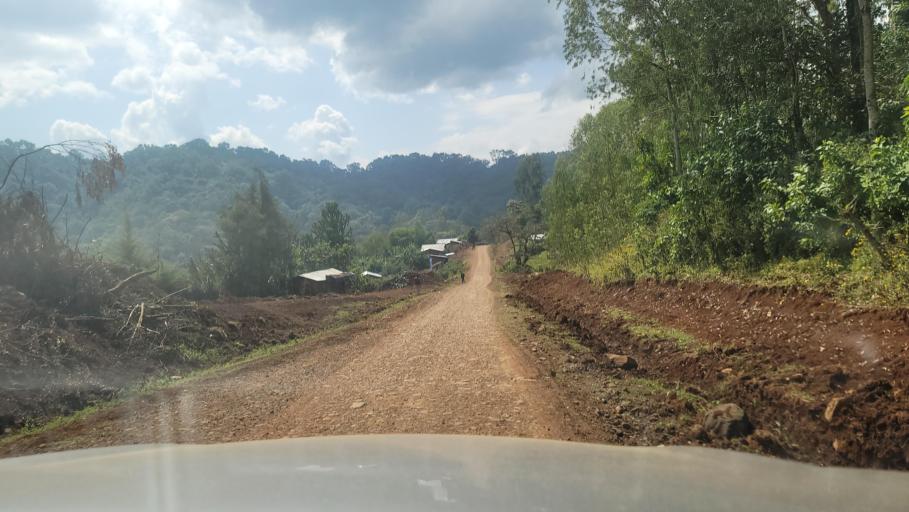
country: ET
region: Southern Nations, Nationalities, and People's Region
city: Bonga
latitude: 7.6935
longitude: 36.2446
